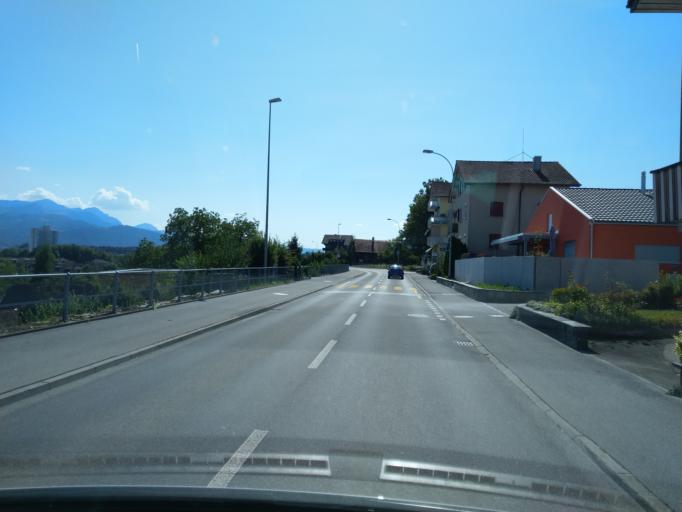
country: CH
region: Lucerne
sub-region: Hochdorf District
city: Emmen
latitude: 47.0993
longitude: 8.2806
